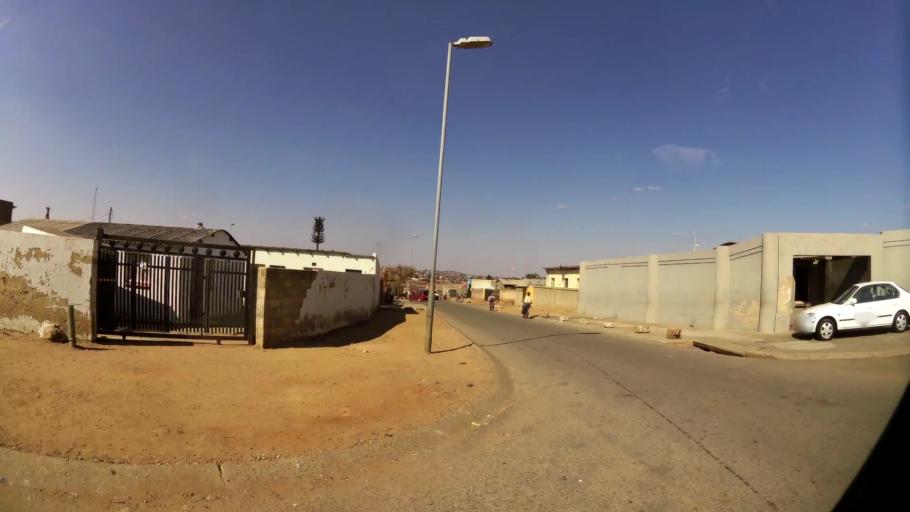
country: ZA
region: Gauteng
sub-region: City of Johannesburg Metropolitan Municipality
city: Soweto
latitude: -26.2315
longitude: 27.8829
